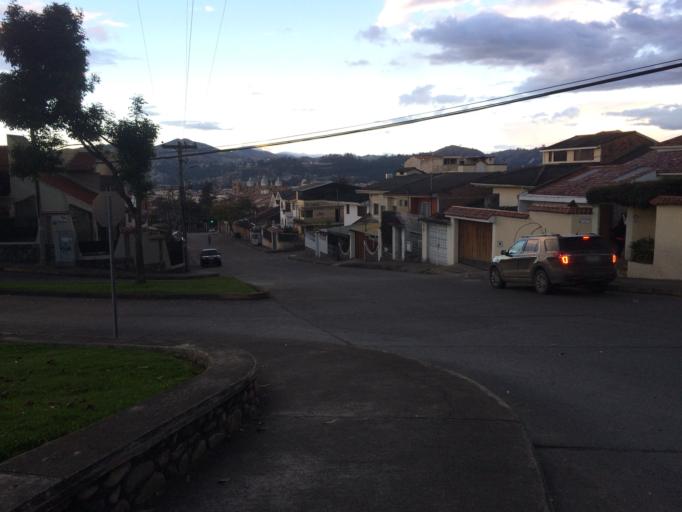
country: EC
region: Azuay
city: Cuenca
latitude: -2.8866
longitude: -79.0047
